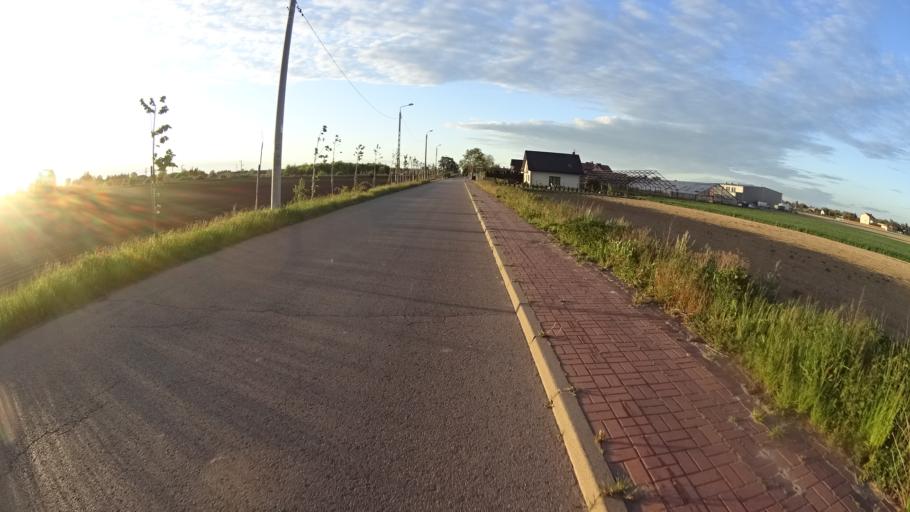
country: PL
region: Masovian Voivodeship
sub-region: Powiat warszawski zachodni
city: Jozefow
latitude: 52.2043
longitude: 20.7447
